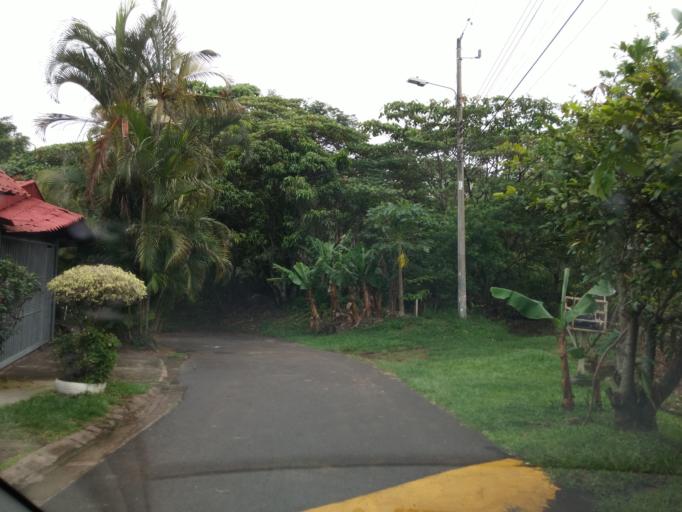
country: CR
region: Heredia
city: Mercedes
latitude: 10.0199
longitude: -84.1499
